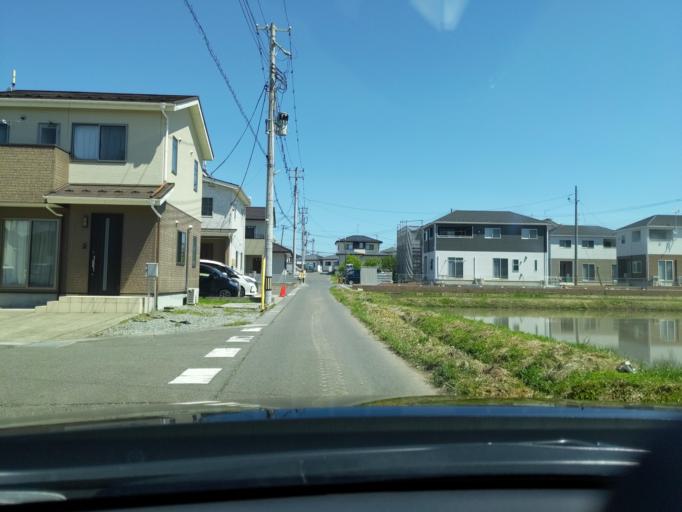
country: JP
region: Fukushima
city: Koriyama
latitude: 37.4158
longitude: 140.4044
